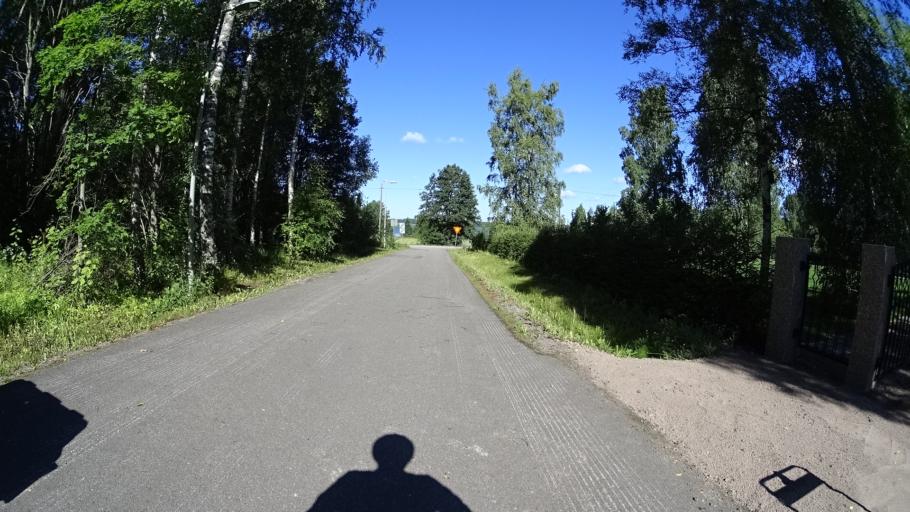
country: FI
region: Uusimaa
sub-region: Helsinki
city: Tuusula
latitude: 60.4342
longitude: 25.0596
